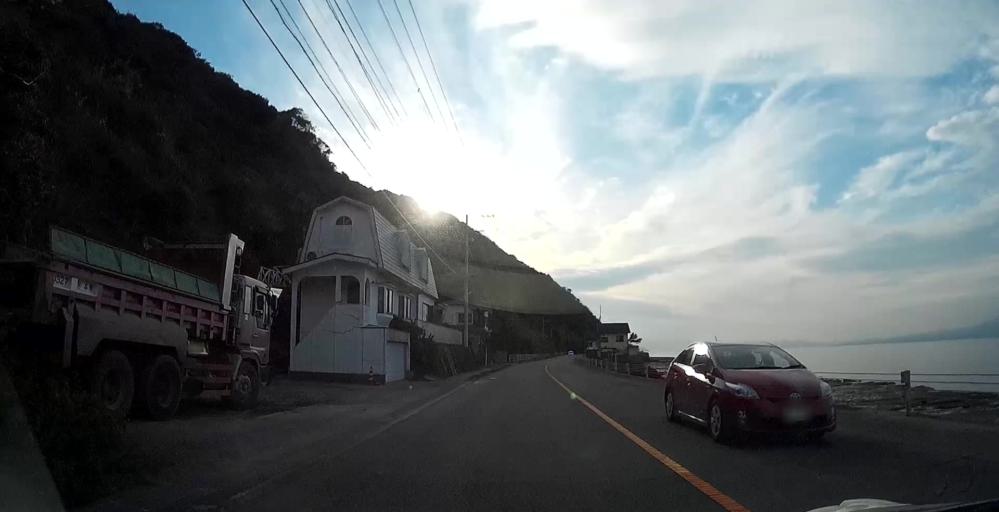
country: JP
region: Kumamoto
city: Matsubase
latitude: 32.6467
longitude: 130.4893
